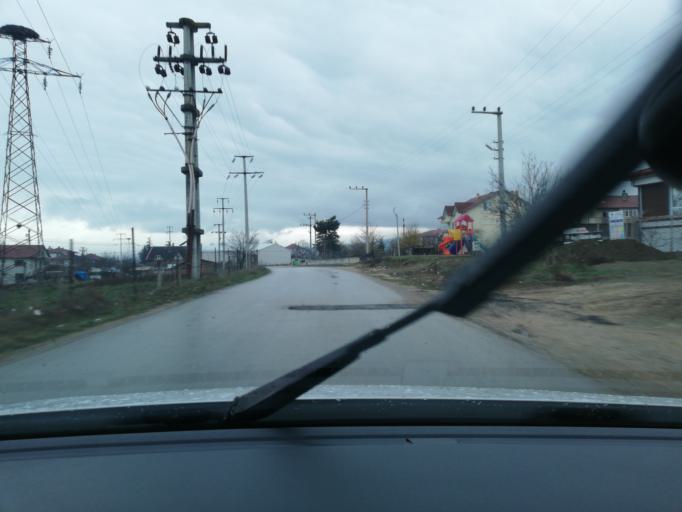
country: TR
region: Bolu
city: Bolu
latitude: 40.7563
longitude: 31.6357
